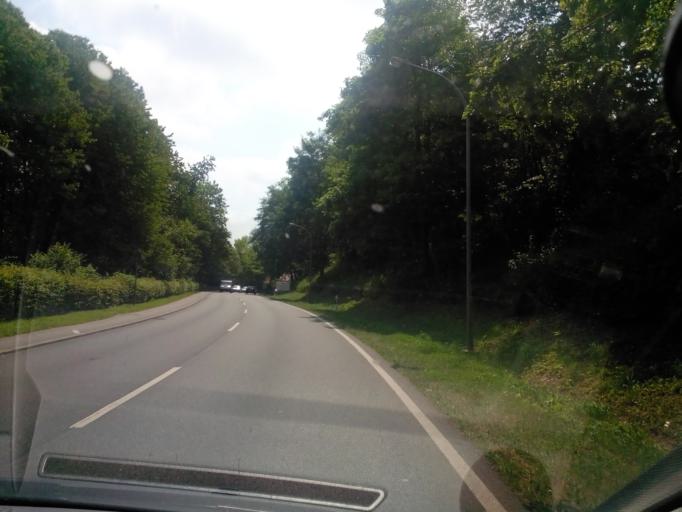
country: DE
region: Saarland
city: Eppelborn
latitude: 49.4080
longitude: 6.9514
